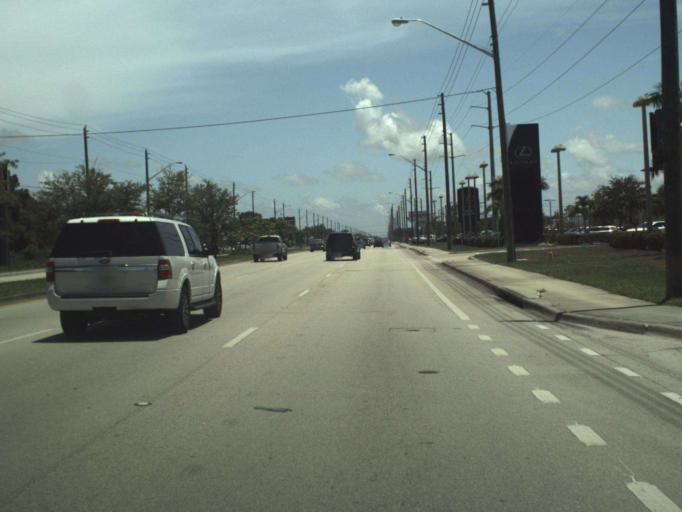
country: US
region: Florida
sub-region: Saint Lucie County
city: White City
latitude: 27.3718
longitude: -80.3260
